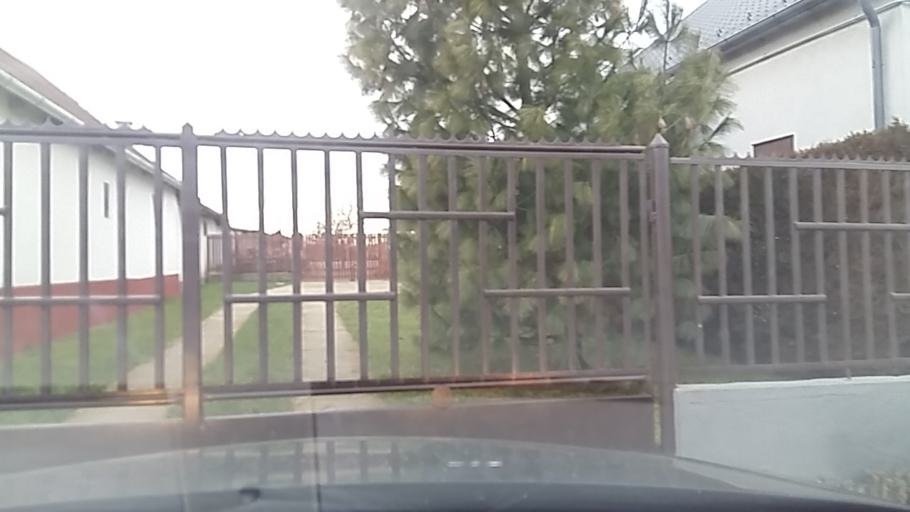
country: HU
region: Szabolcs-Szatmar-Bereg
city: Kek
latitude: 48.1082
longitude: 21.8815
